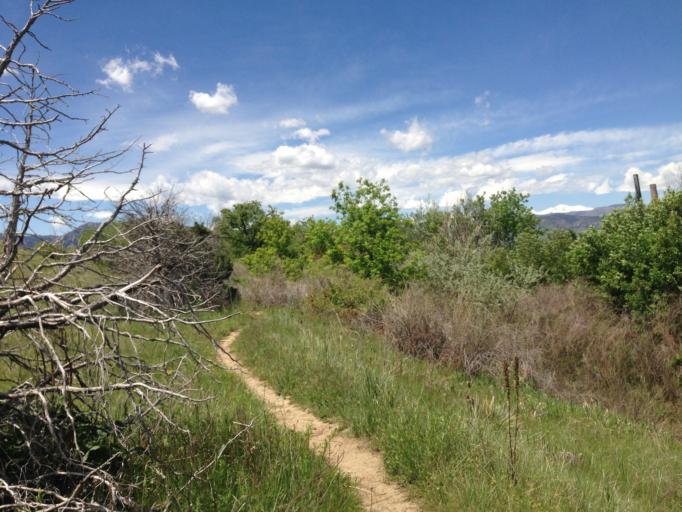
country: US
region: Colorado
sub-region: Boulder County
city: Gunbarrel
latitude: 40.0162
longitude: -105.1918
